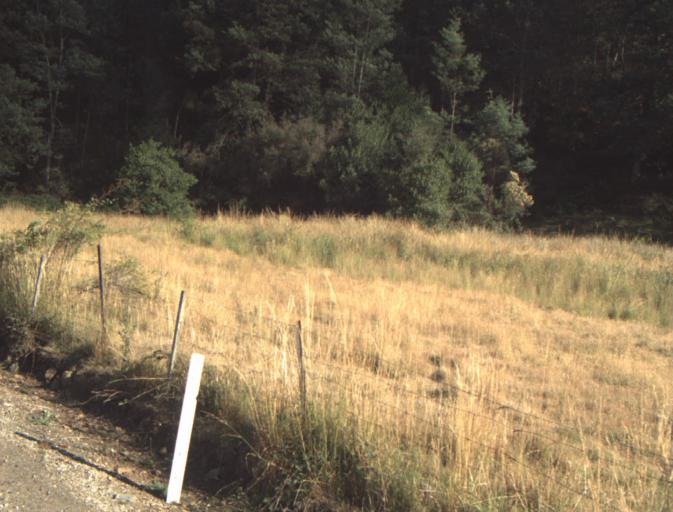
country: AU
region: Tasmania
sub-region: Launceston
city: Mayfield
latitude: -41.2905
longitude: 147.2029
